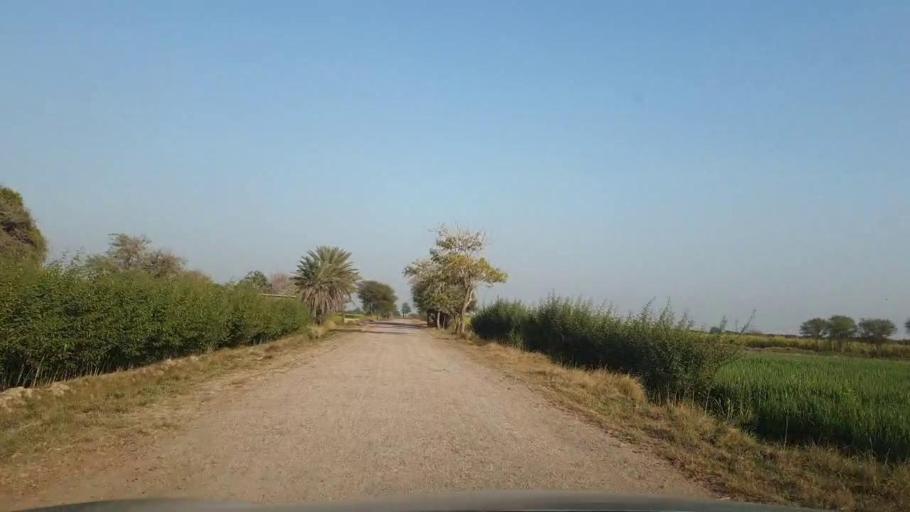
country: PK
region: Sindh
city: Tando Allahyar
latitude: 25.5864
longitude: 68.6729
